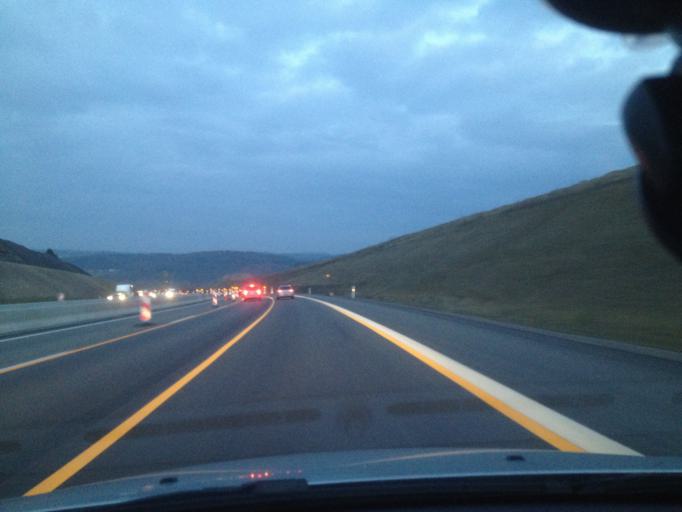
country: DE
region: Baden-Wuerttemberg
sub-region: Karlsruhe Region
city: Konigsbach-Stein
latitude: 48.9337
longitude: 8.5512
